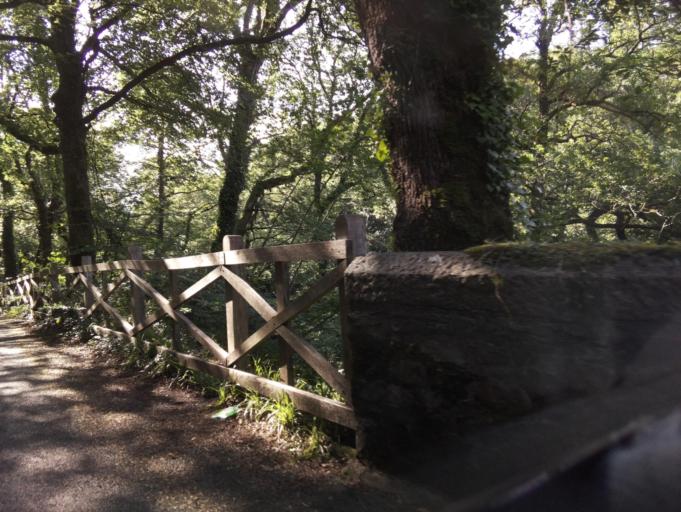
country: GB
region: England
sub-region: Devon
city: Ashburton
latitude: 50.5211
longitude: -3.7926
